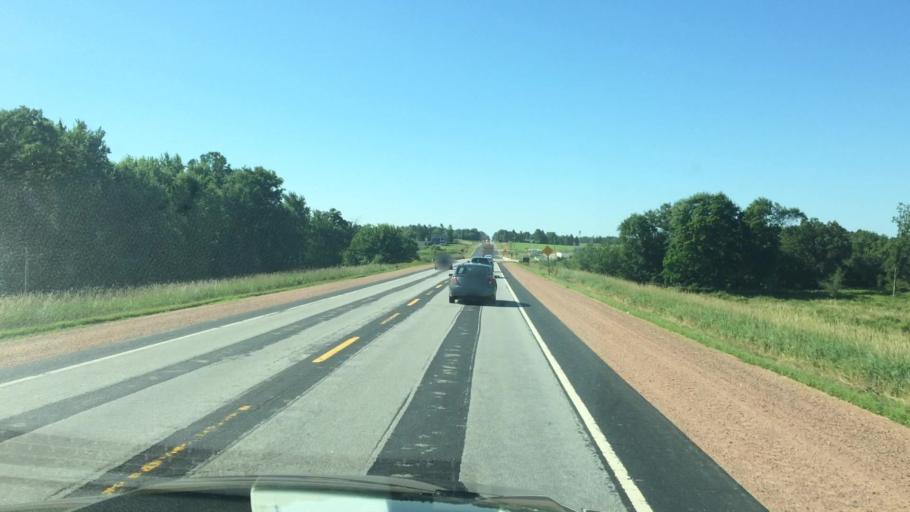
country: US
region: Wisconsin
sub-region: Marathon County
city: Stratford
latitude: 44.8237
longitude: -90.0792
